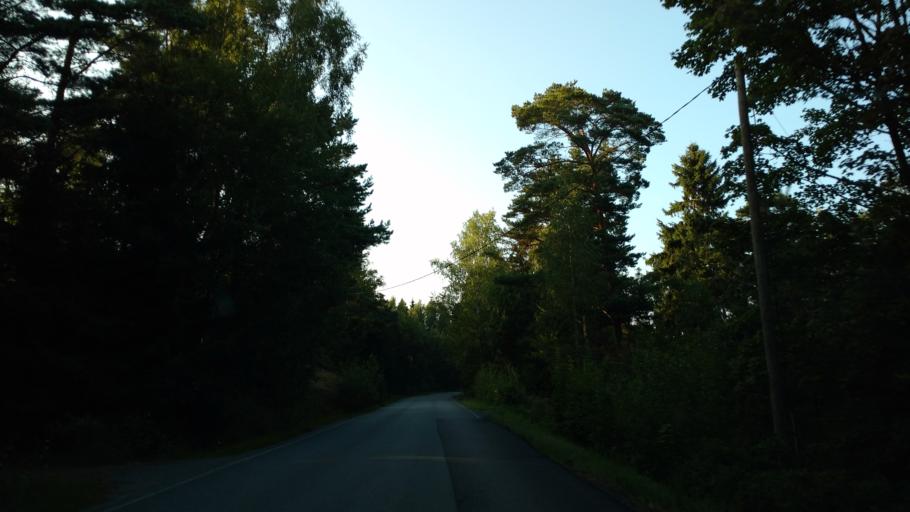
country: FI
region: Varsinais-Suomi
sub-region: Aboland-Turunmaa
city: Dragsfjaerd
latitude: 59.9765
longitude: 22.4493
